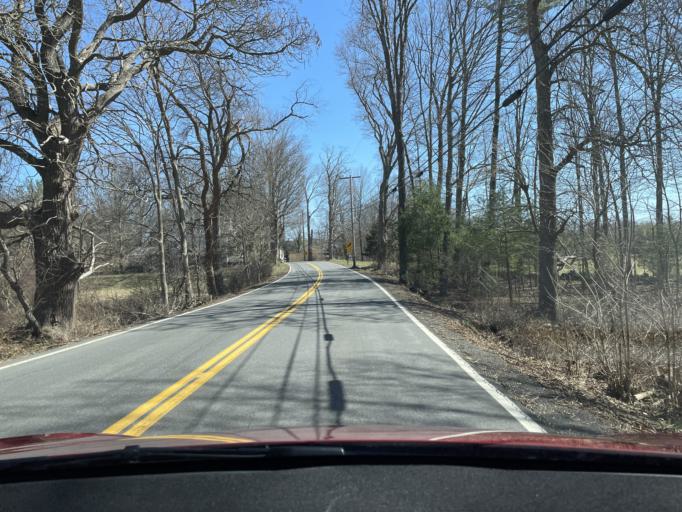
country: US
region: New York
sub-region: Ulster County
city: Zena
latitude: 42.0520
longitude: -74.0223
